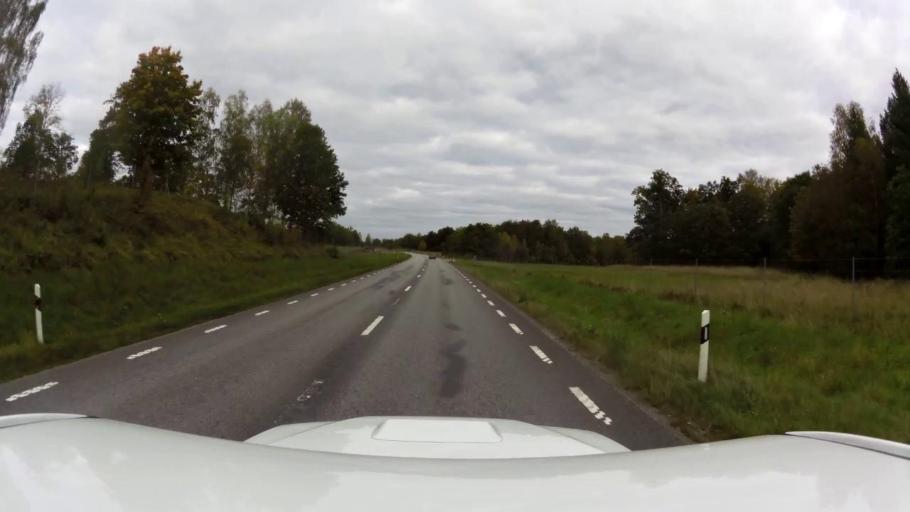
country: SE
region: OEstergoetland
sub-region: Kinda Kommun
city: Rimforsa
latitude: 58.2185
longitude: 15.6643
